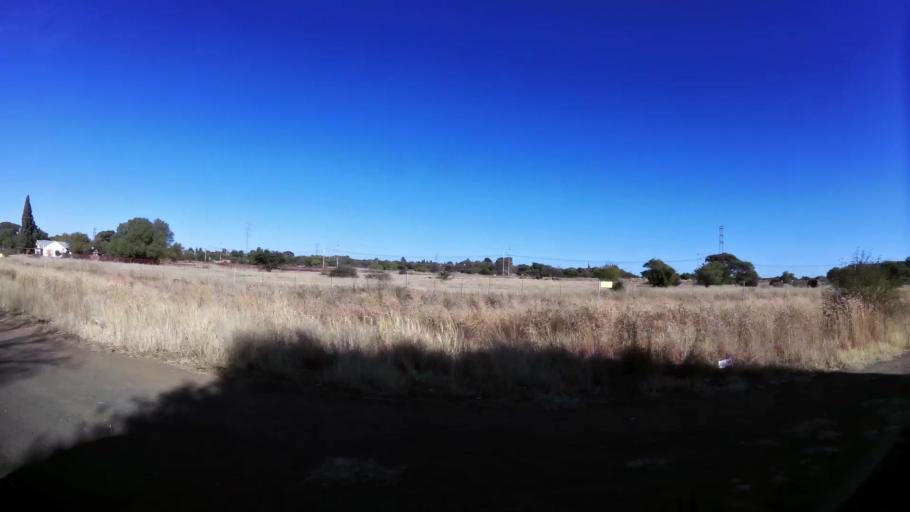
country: ZA
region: Northern Cape
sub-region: Frances Baard District Municipality
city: Kimberley
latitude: -28.7433
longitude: 24.7916
